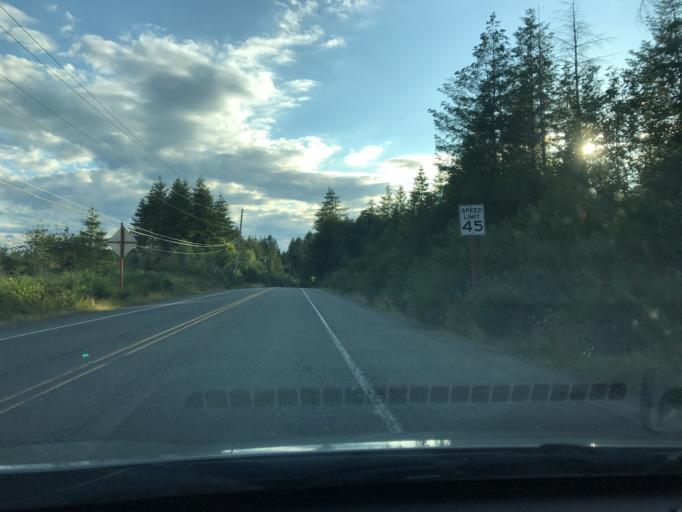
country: US
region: Washington
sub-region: King County
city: Black Diamond
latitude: 47.3112
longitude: -122.0341
